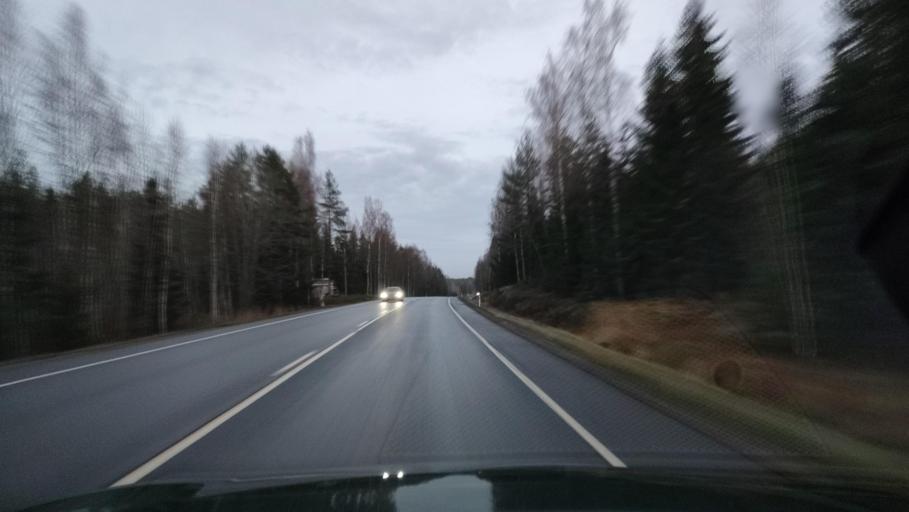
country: FI
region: Ostrobothnia
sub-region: Vaasa
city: Ristinummi
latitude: 62.9779
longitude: 21.7692
